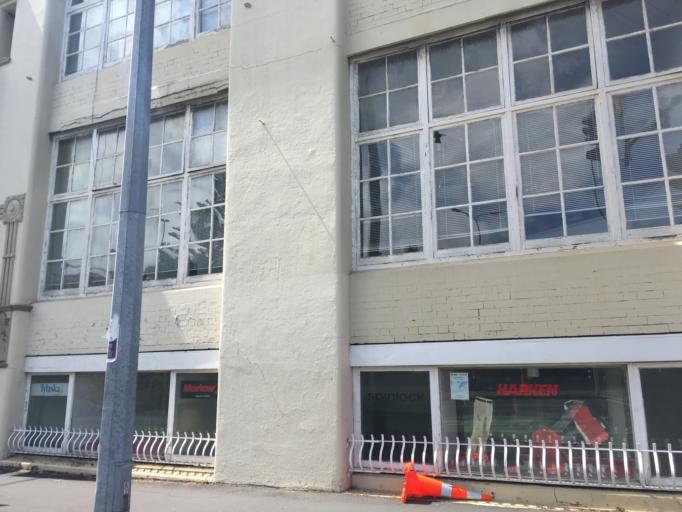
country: NZ
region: Auckland
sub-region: Auckland
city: Auckland
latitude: -36.8445
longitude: 174.7635
